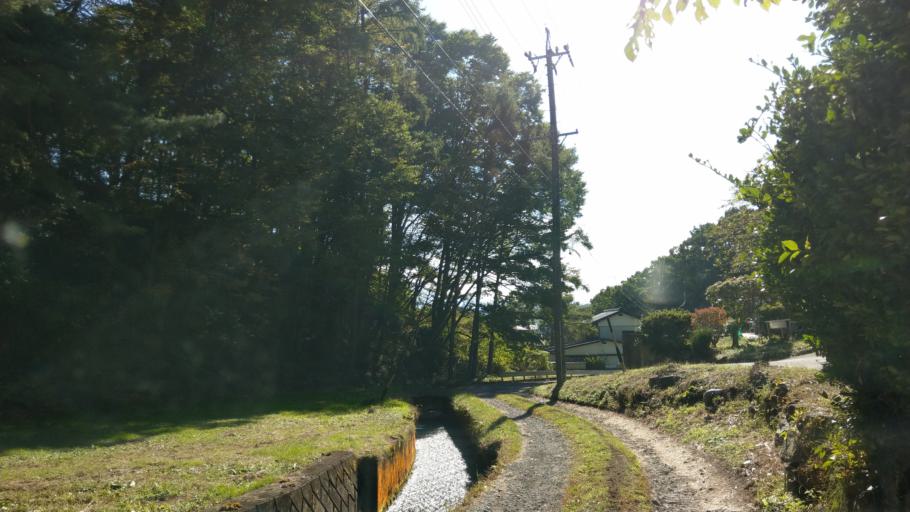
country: JP
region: Nagano
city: Komoro
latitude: 36.3374
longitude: 138.4344
